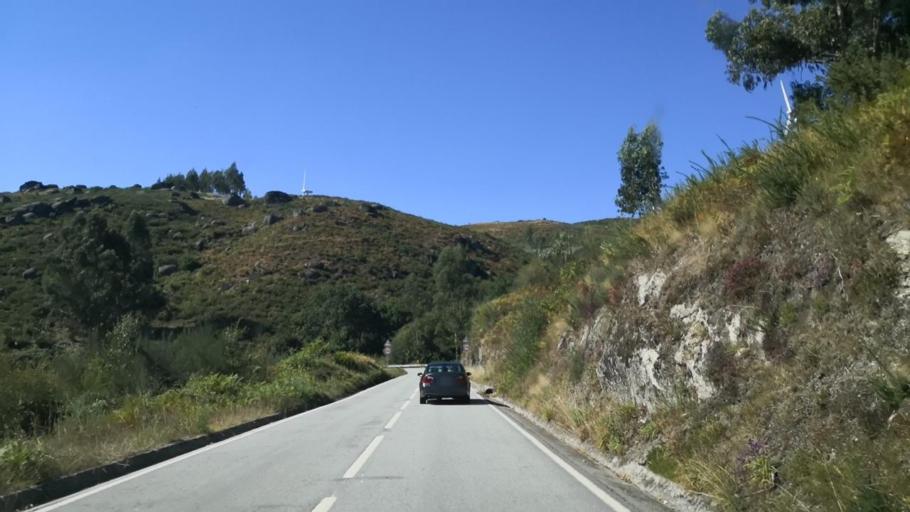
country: PT
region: Braga
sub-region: Fafe
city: Fafe
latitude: 41.4964
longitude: -8.0862
